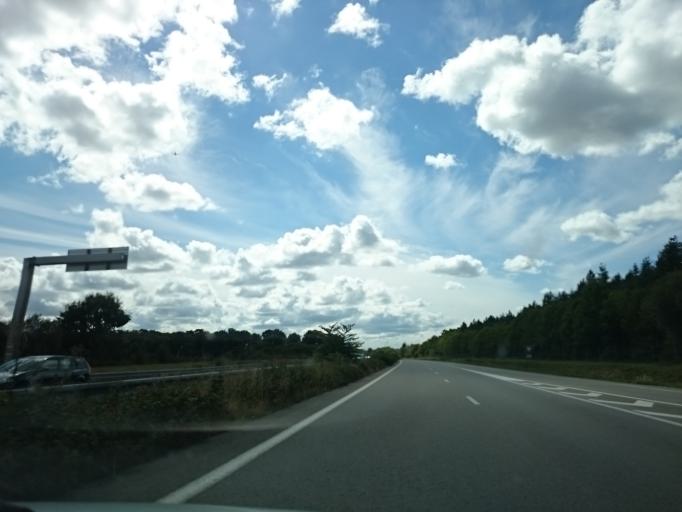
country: FR
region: Pays de la Loire
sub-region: Departement de la Loire-Atlantique
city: Saint-Mars-du-Desert
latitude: 47.3380
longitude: -1.3859
